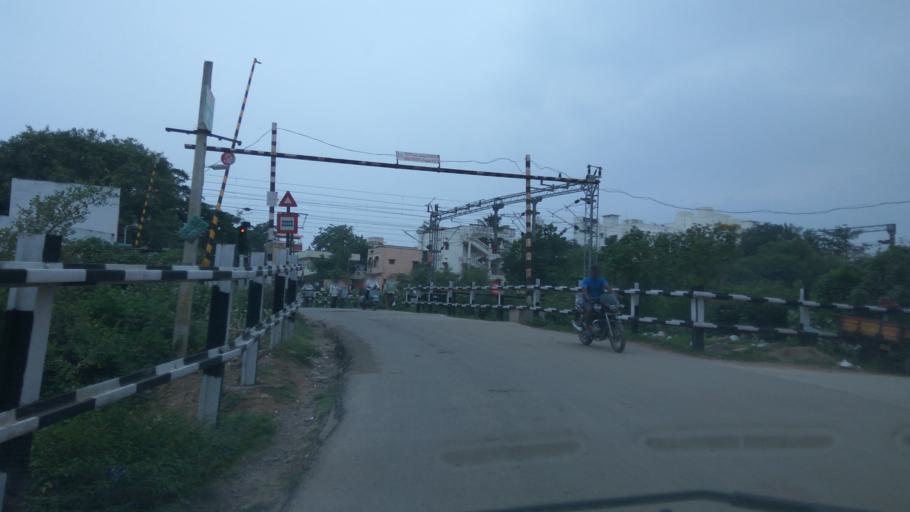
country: IN
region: Telangana
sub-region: Hyderabad
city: Malkajgiri
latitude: 17.4517
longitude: 78.5308
